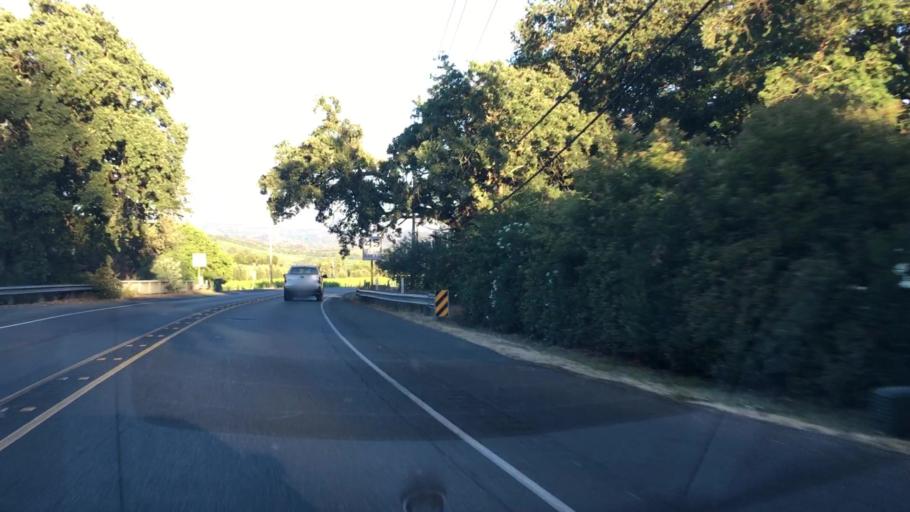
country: US
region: California
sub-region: Sonoma County
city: Kenwood
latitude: 38.4278
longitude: -122.5602
